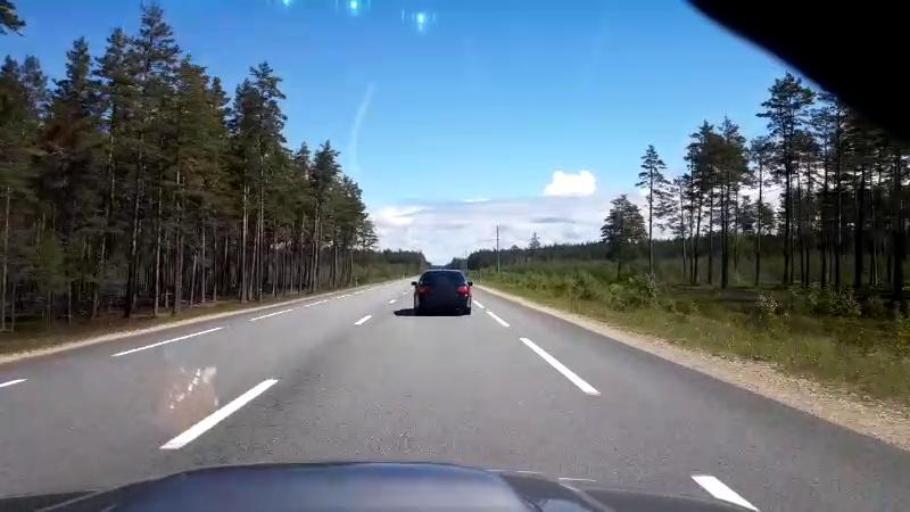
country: LV
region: Saulkrastu
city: Saulkrasti
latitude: 57.2147
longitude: 24.3980
